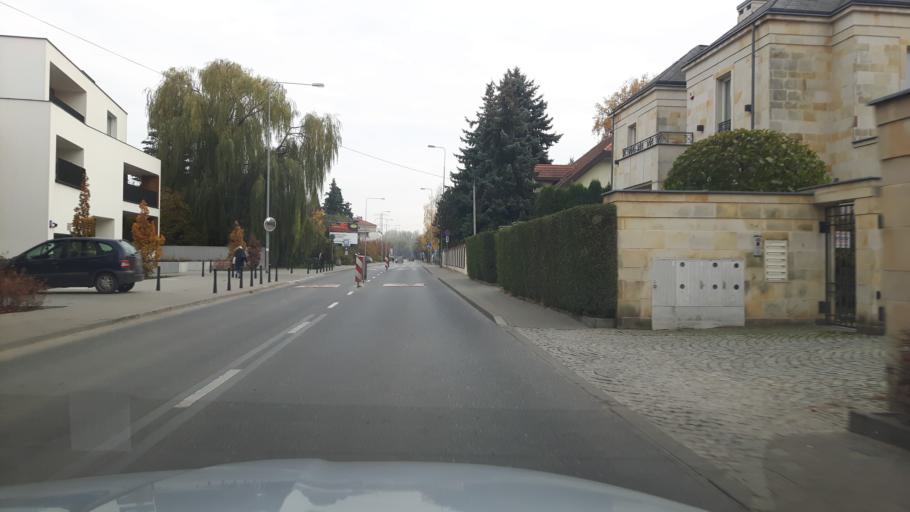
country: PL
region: Masovian Voivodeship
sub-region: Warszawa
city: Wilanow
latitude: 52.1692
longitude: 21.1070
